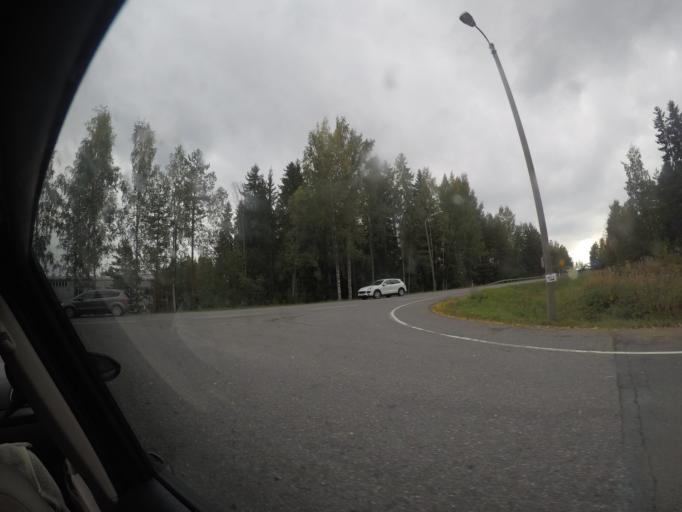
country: FI
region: Pirkanmaa
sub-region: Tampere
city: Kangasala
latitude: 61.4487
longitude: 24.1047
